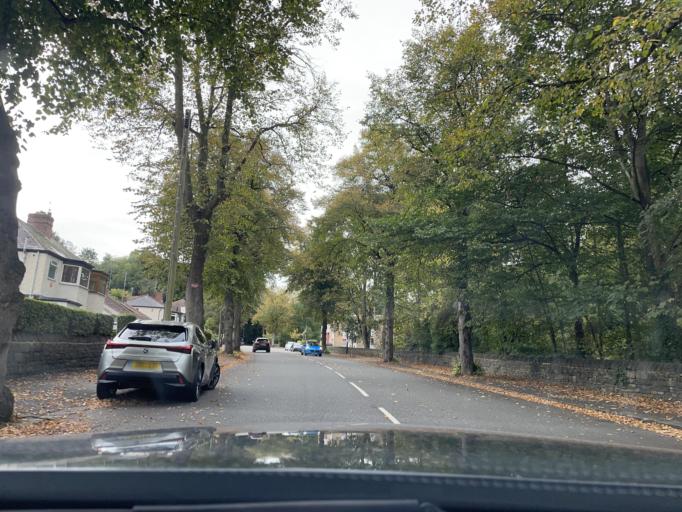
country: GB
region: England
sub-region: Sheffield
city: Oughtibridge
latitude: 53.3990
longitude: -1.5114
